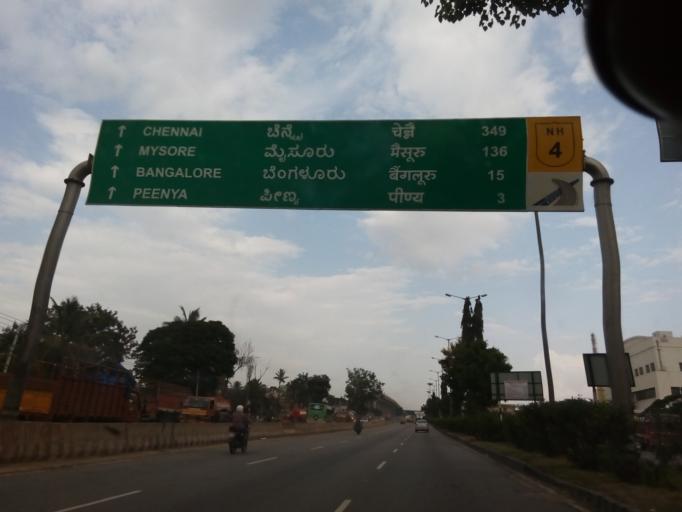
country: IN
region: Karnataka
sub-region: Bangalore Rural
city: Nelamangala
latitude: 13.0507
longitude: 77.4919
